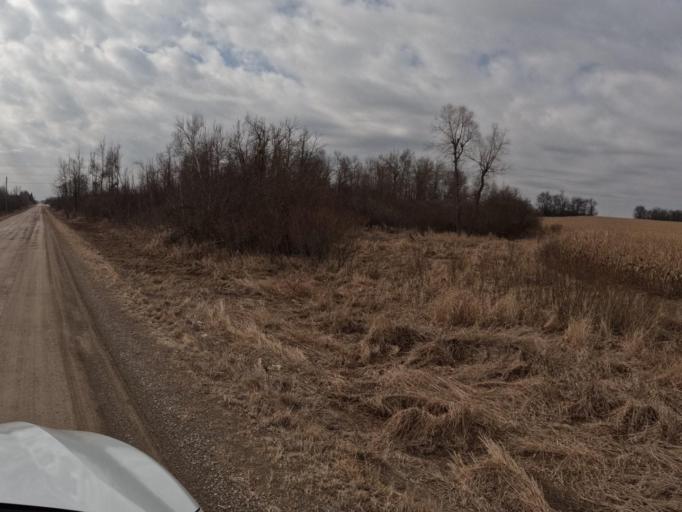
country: CA
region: Ontario
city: Orangeville
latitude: 43.9383
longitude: -80.2220
